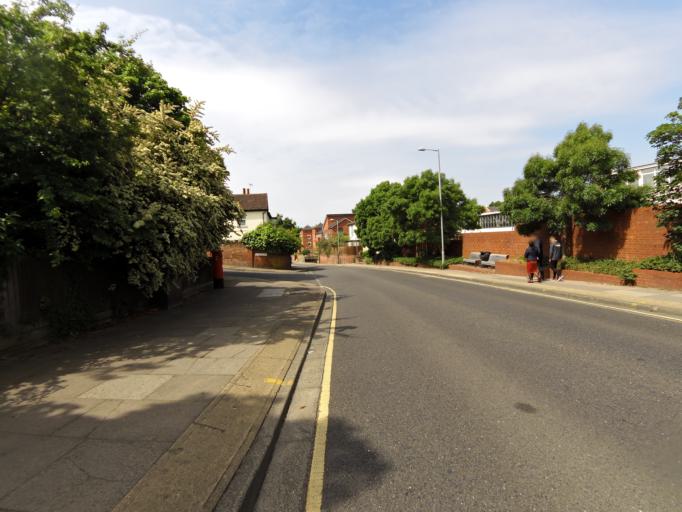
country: GB
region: England
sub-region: Suffolk
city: Ipswich
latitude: 52.0611
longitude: 1.1723
